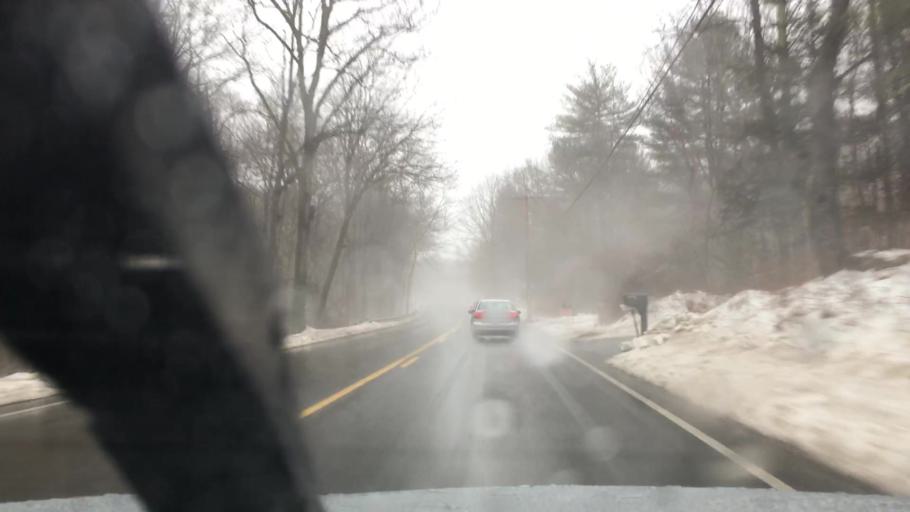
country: US
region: Massachusetts
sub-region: Hampshire County
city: Granby
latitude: 42.2430
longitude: -72.4798
